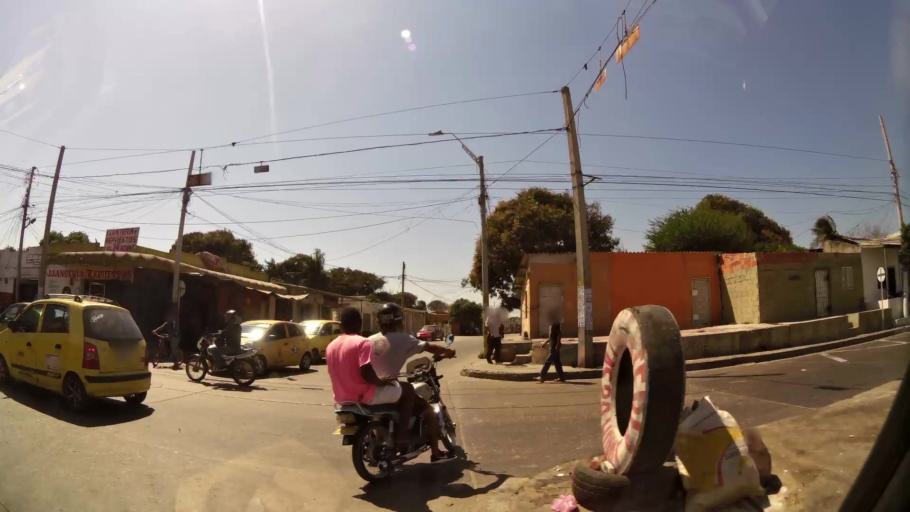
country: CO
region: Atlantico
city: Barranquilla
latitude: 10.9608
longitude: -74.7749
